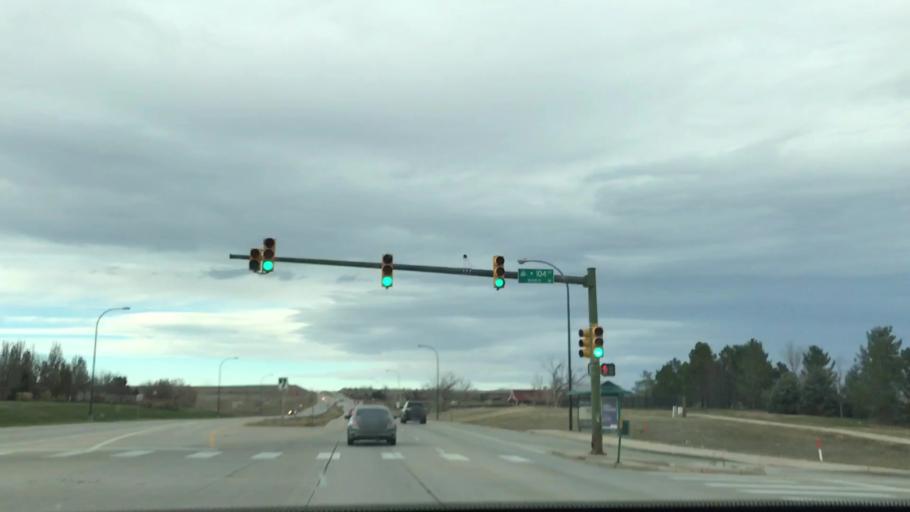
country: US
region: Colorado
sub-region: Broomfield County
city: Broomfield
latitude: 39.8854
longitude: -105.0962
